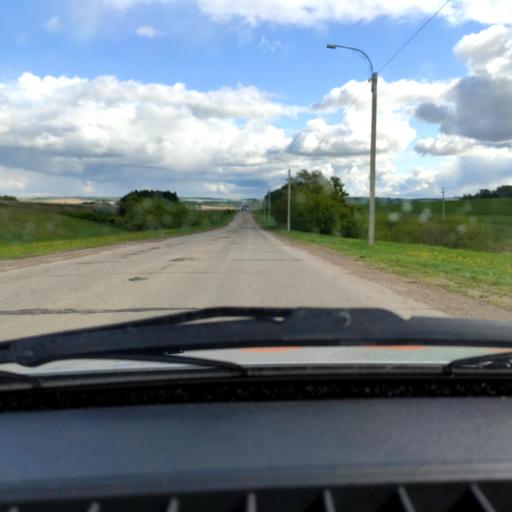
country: RU
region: Bashkortostan
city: Tolbazy
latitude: 53.9713
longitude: 55.9117
